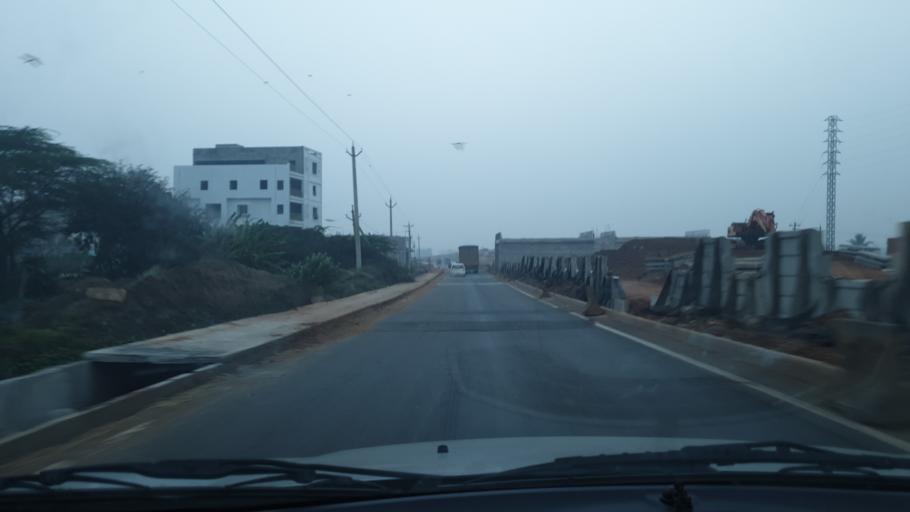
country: IN
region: Andhra Pradesh
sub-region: Srikakulam
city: Narasannapeta
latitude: 18.4223
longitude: 84.0447
